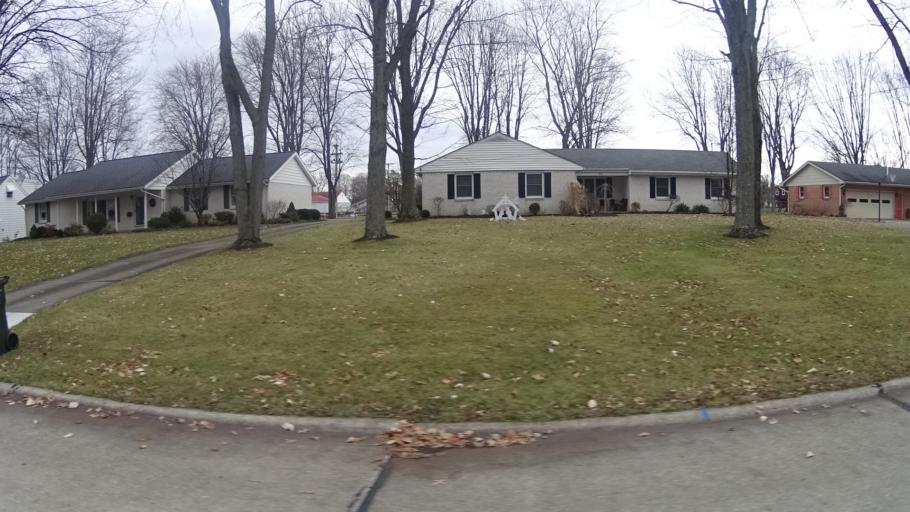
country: US
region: Ohio
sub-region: Lorain County
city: Wellington
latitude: 41.1636
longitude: -82.2137
